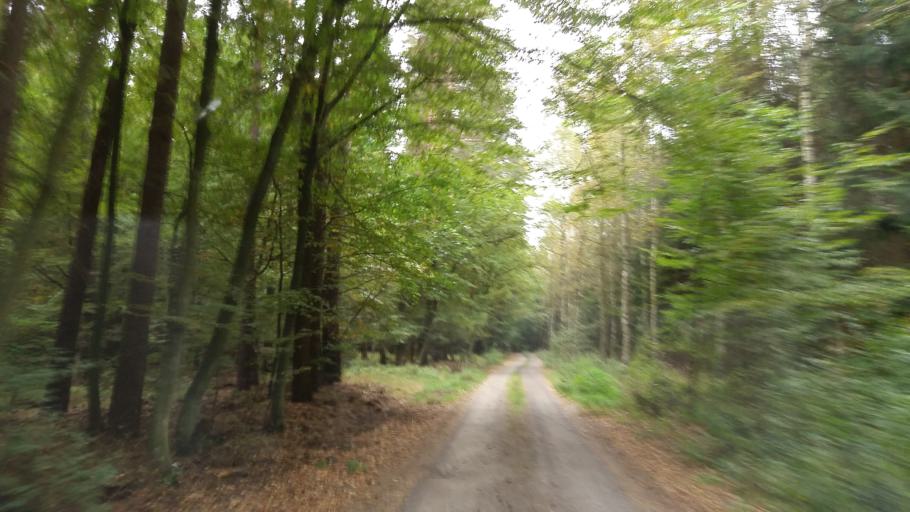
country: PL
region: West Pomeranian Voivodeship
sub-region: Powiat choszczenski
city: Pelczyce
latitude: 52.9633
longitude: 15.3197
